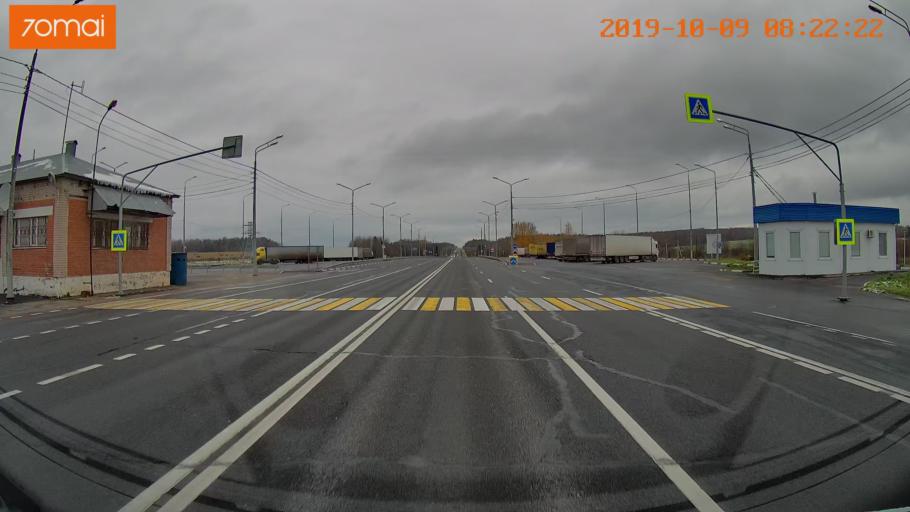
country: RU
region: Vologda
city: Gryazovets
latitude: 58.7422
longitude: 40.2889
